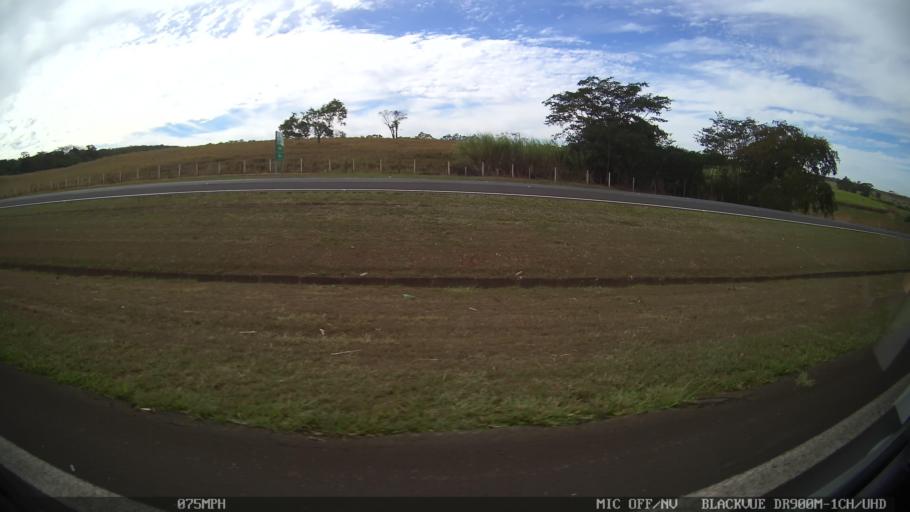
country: BR
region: Sao Paulo
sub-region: Santa Adelia
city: Santa Adelia
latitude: -21.2841
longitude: -48.8527
